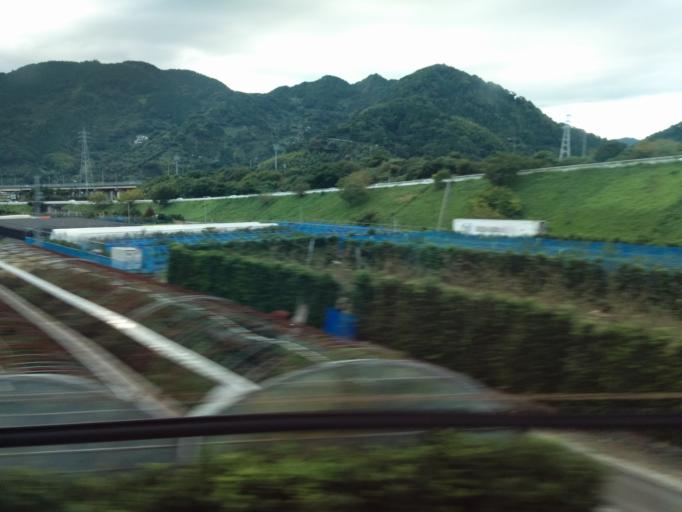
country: JP
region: Shizuoka
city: Shizuoka-shi
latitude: 34.9273
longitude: 138.3619
